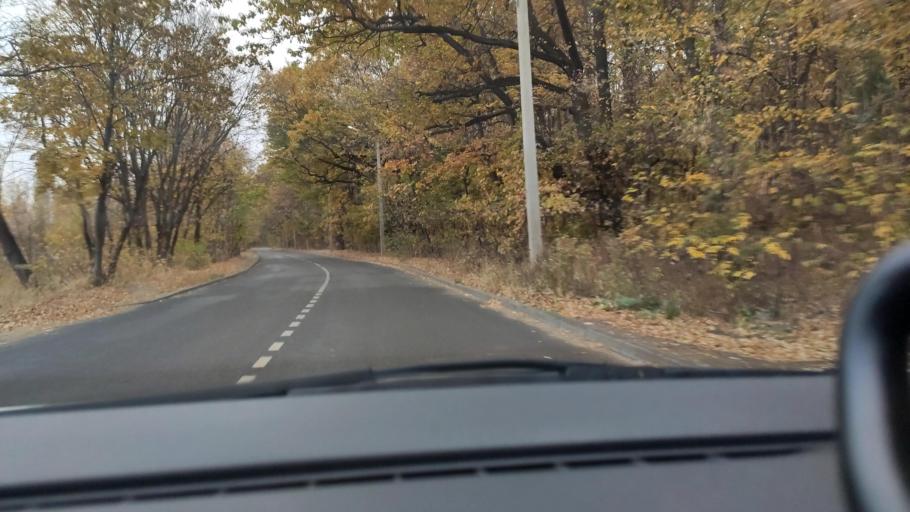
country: RU
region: Voronezj
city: Voronezh
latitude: 51.7248
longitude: 39.2348
